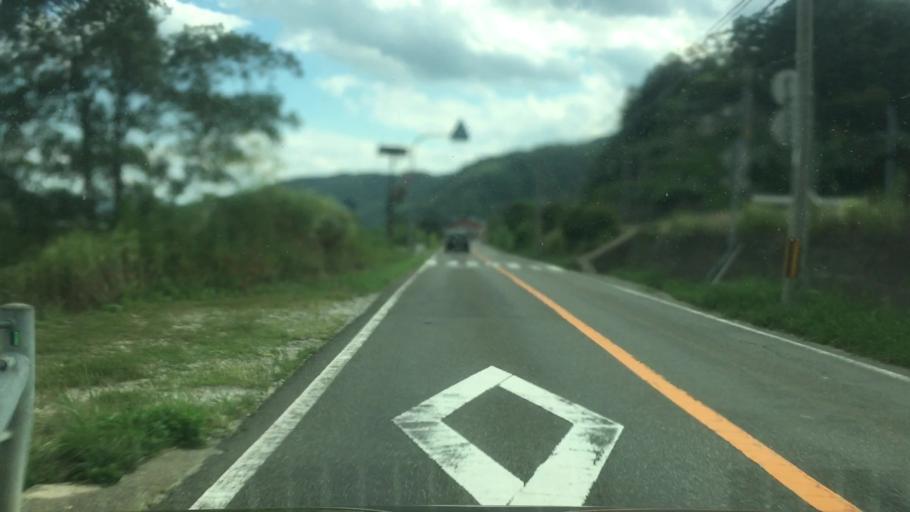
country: JP
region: Hyogo
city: Toyooka
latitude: 35.5966
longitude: 134.8016
